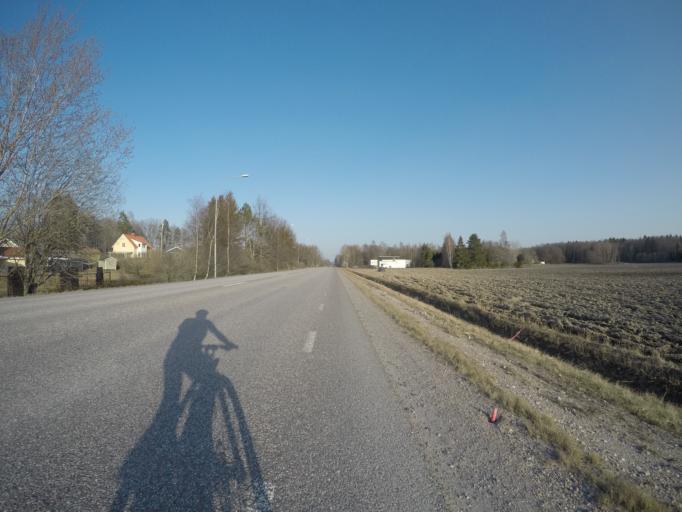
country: SE
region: Vaestmanland
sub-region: Kungsors Kommun
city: Kungsoer
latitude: 59.4222
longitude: 16.1424
